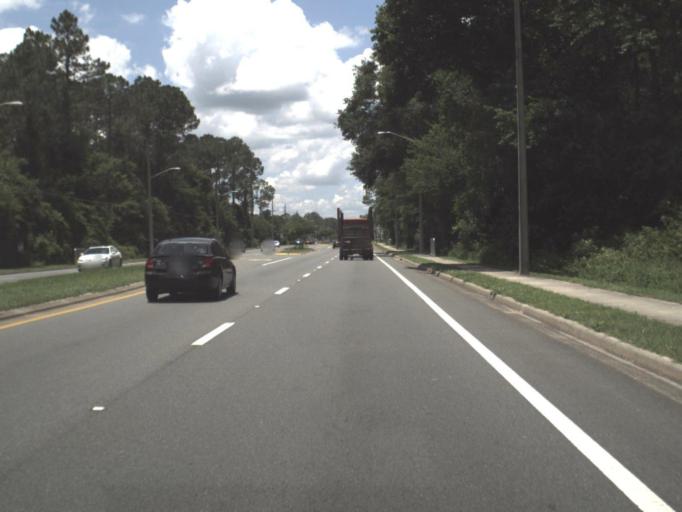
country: US
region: Florida
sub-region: Alachua County
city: Gainesville
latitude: 29.6885
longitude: -82.3139
